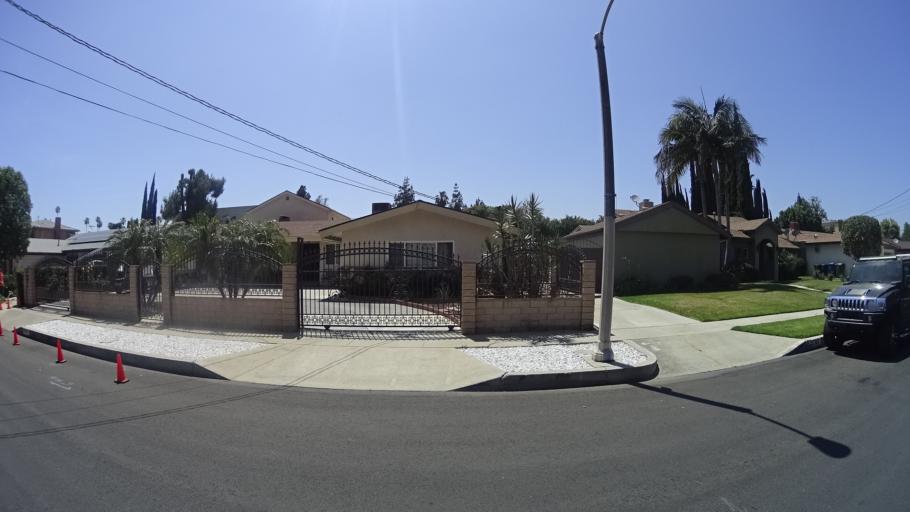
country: US
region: California
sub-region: Los Angeles County
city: Van Nuys
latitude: 34.1922
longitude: -118.4455
